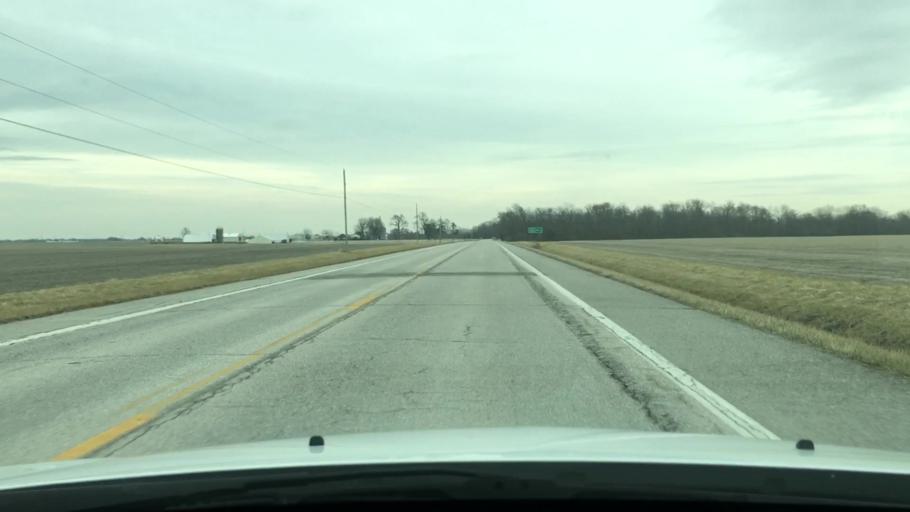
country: US
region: Missouri
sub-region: Audrain County
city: Vandalia
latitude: 39.2791
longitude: -91.5716
